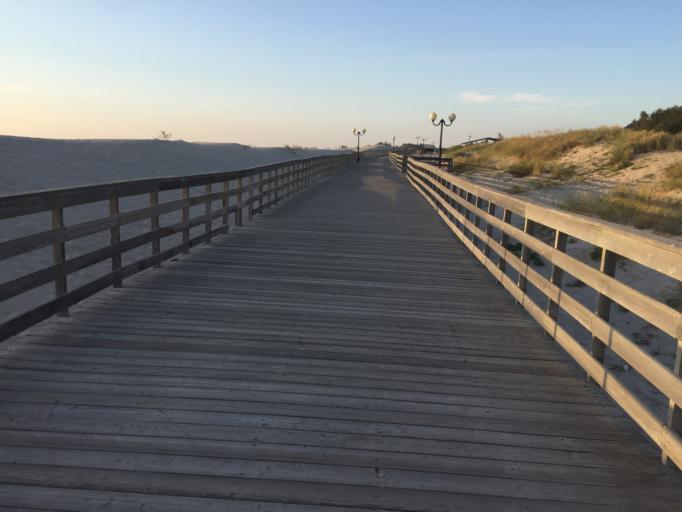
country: RU
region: Kaliningrad
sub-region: Gorod Kaliningrad
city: Yantarnyy
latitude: 54.8730
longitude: 19.9334
